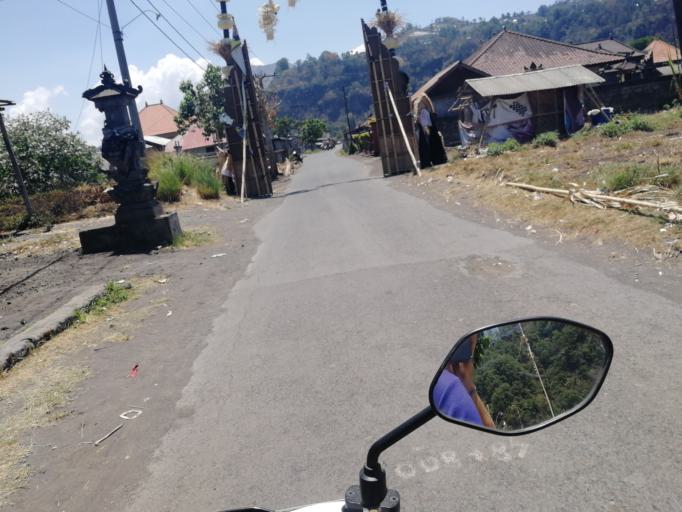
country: ID
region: Bali
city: Banjar Trunyan
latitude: -8.2221
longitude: 115.4154
